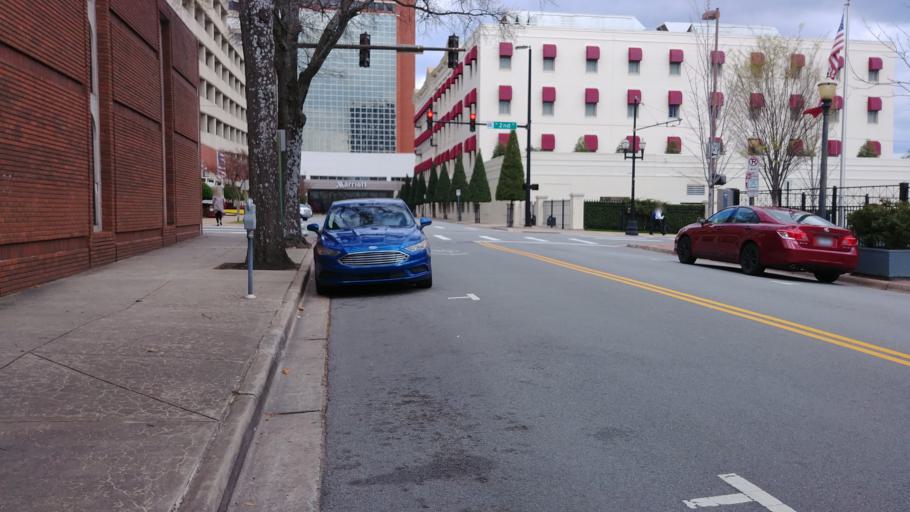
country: US
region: Arkansas
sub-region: Pulaski County
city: Little Rock
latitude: 34.7469
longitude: -92.2718
